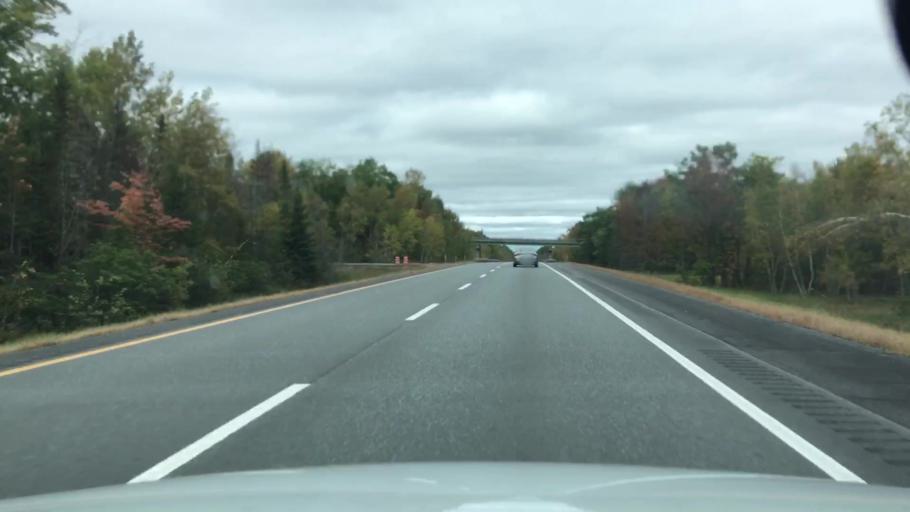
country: US
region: Maine
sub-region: Waldo County
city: Burnham
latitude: 44.7337
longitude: -69.4335
